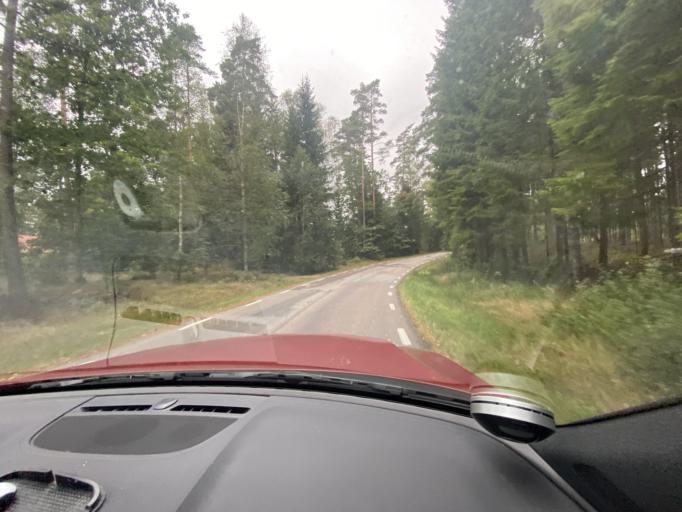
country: SE
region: Kronoberg
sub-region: Markaryds Kommun
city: Markaryd
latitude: 56.4976
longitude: 13.5689
